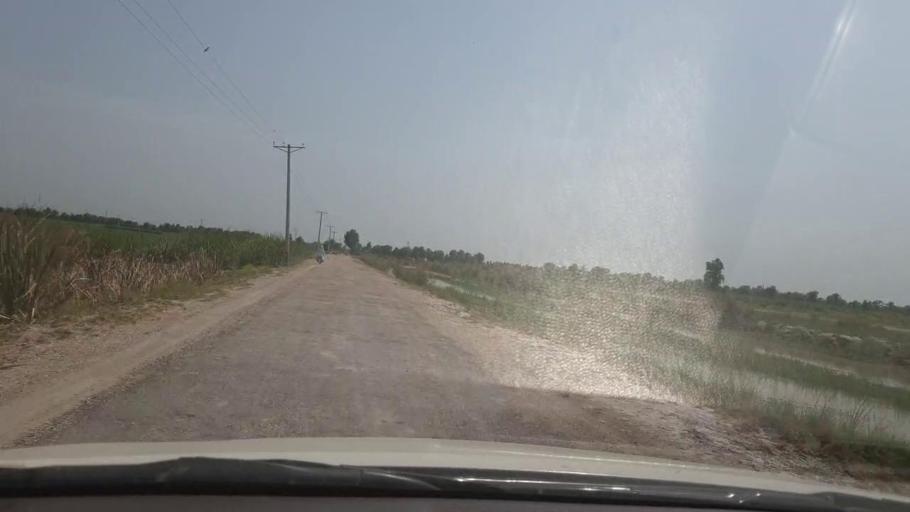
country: PK
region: Sindh
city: Garhi Yasin
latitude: 27.9801
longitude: 68.5027
